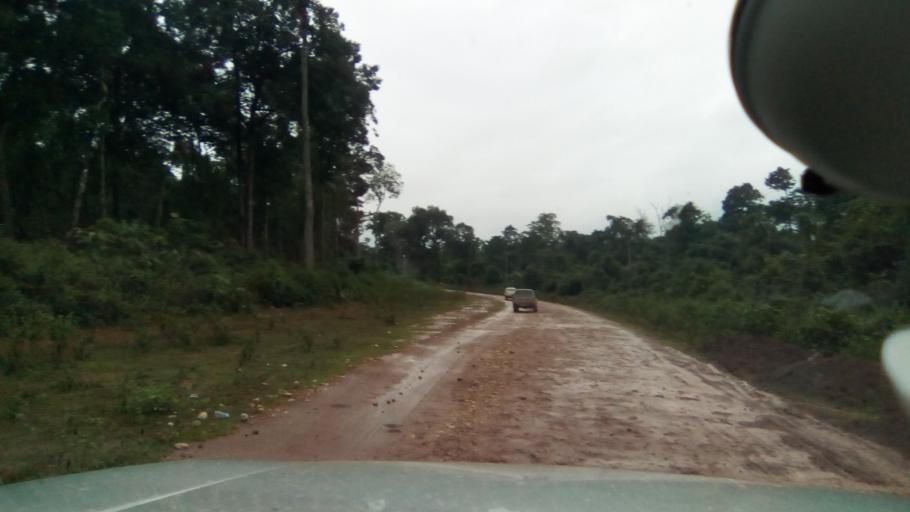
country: LA
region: Attapu
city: Attapu
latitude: 14.6791
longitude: 106.5588
